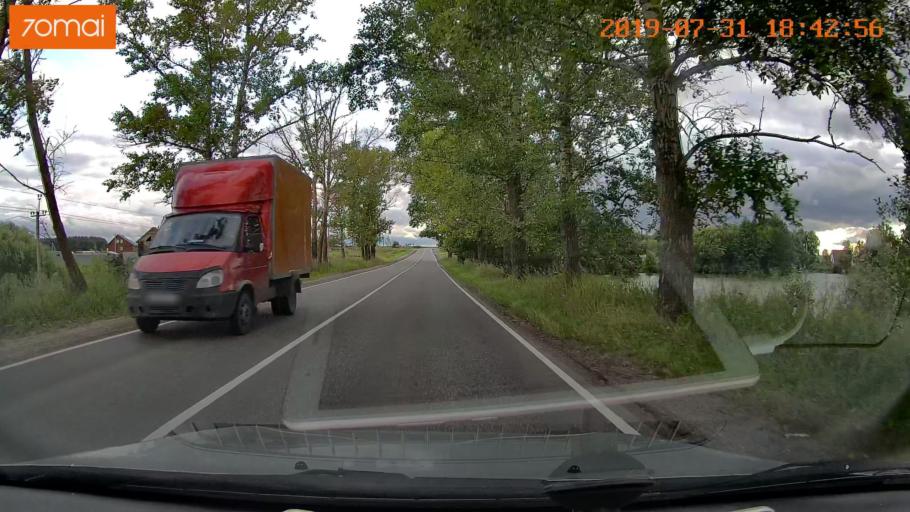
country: RU
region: Moskovskaya
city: Troitskoye
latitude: 55.2460
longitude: 38.5807
